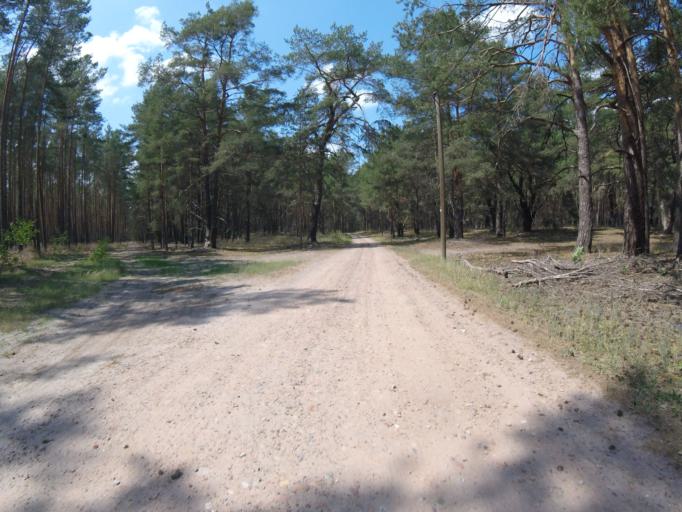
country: DE
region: Brandenburg
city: Bestensee
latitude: 52.2495
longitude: 13.6857
